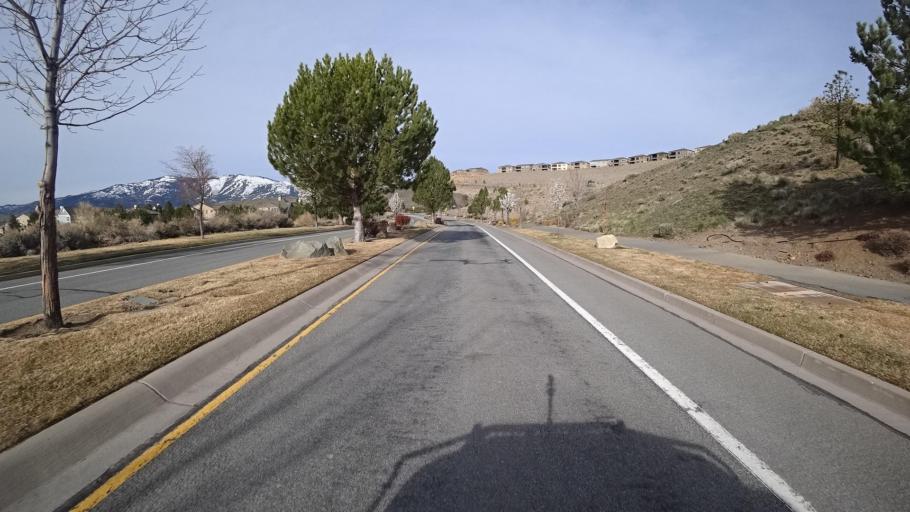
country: US
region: Nevada
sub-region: Washoe County
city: Mogul
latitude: 39.5357
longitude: -119.9472
